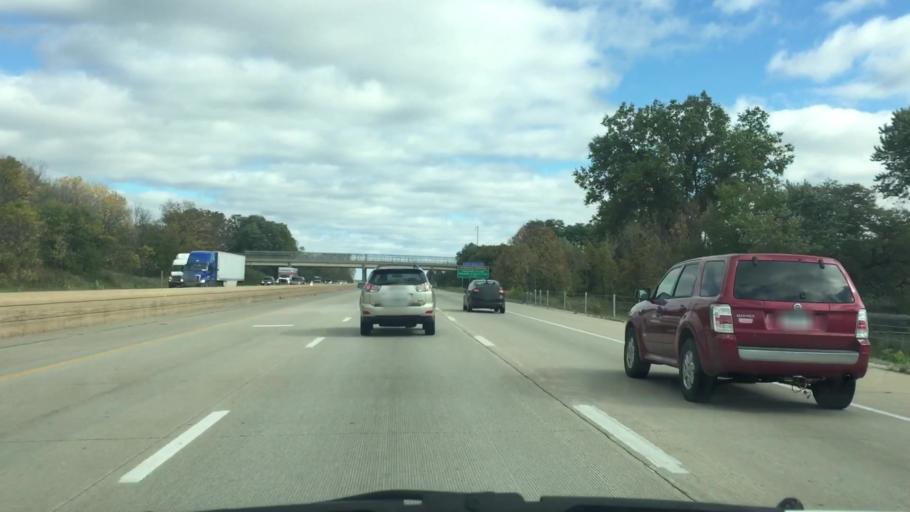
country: US
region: Iowa
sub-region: Johnson County
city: Coralville
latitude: 41.6898
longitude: -91.5848
